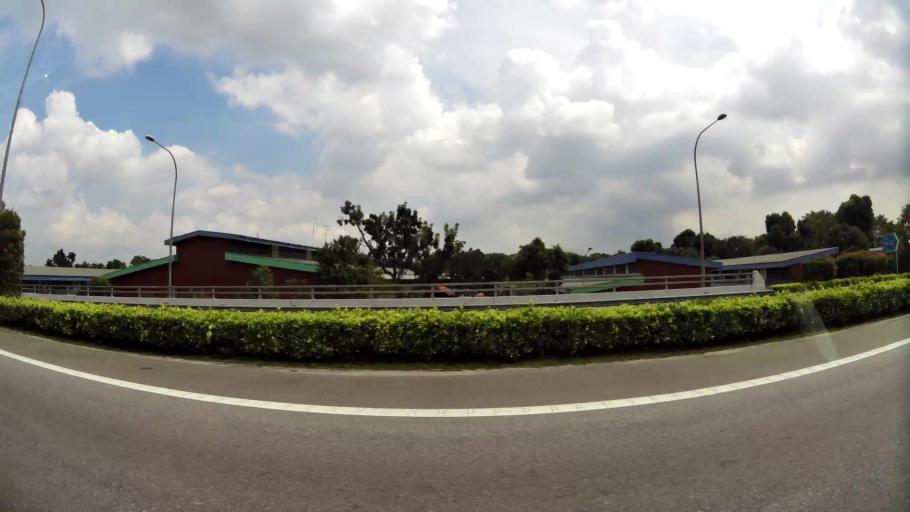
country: SG
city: Singapore
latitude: 1.3736
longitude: 103.8596
